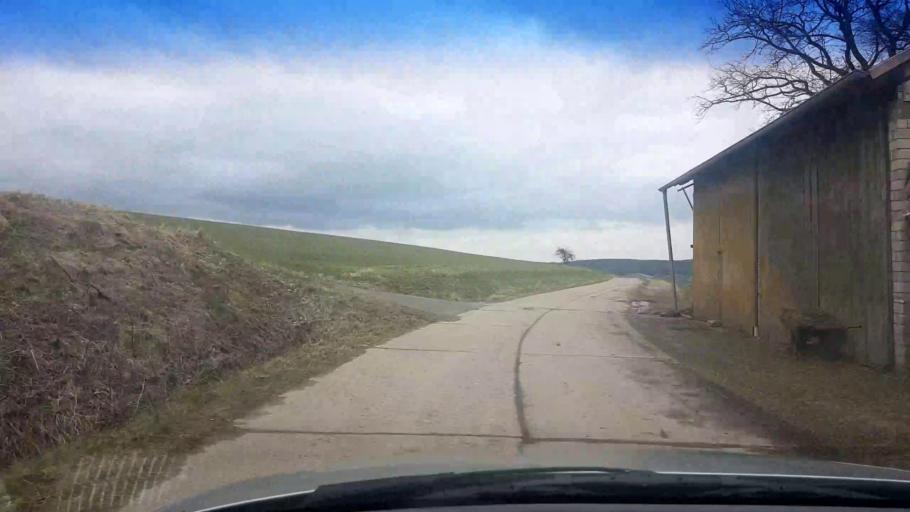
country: DE
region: Bavaria
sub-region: Regierungsbezirk Unterfranken
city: Stettfeld
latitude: 49.9436
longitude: 10.7148
